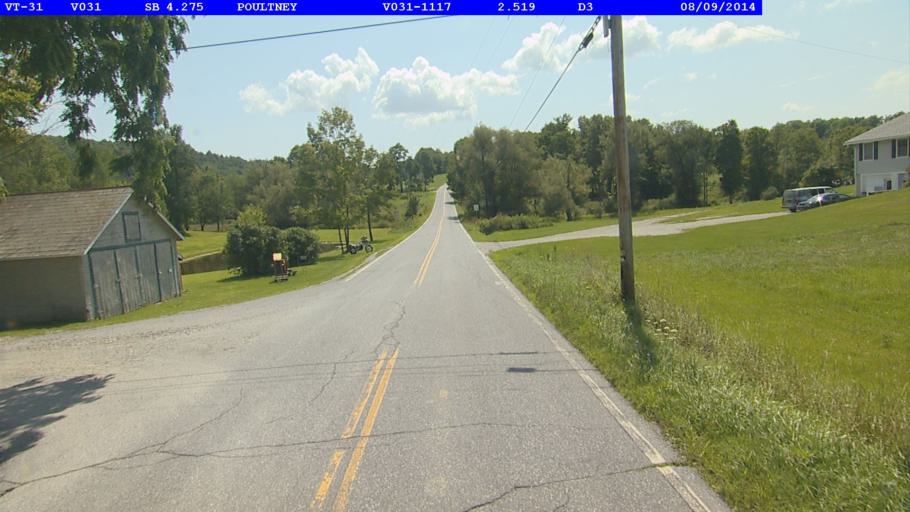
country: US
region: Vermont
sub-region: Rutland County
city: Poultney
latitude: 43.4978
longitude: -73.2367
